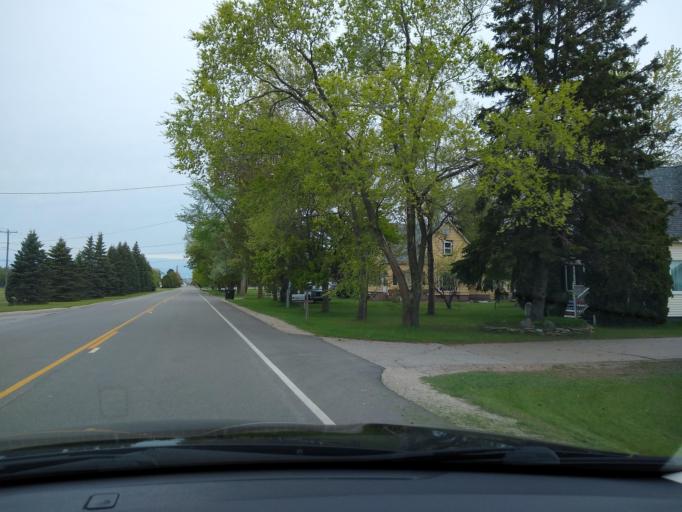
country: US
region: Michigan
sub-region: Delta County
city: Escanaba
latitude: 45.7830
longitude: -87.0761
